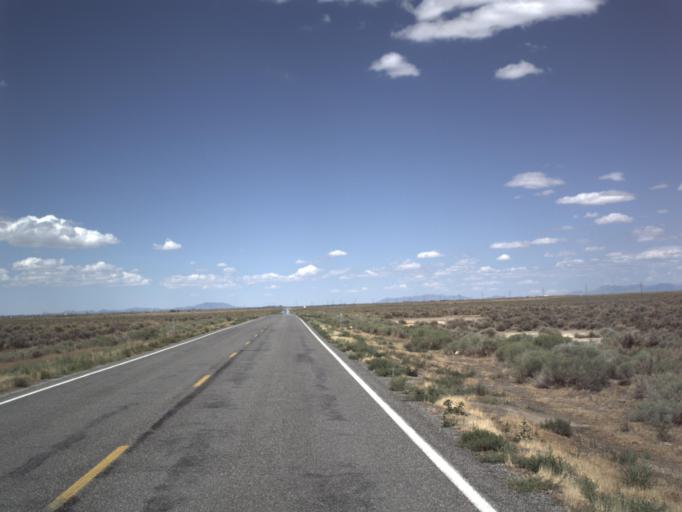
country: US
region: Utah
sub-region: Millard County
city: Delta
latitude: 39.2725
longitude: -112.4552
